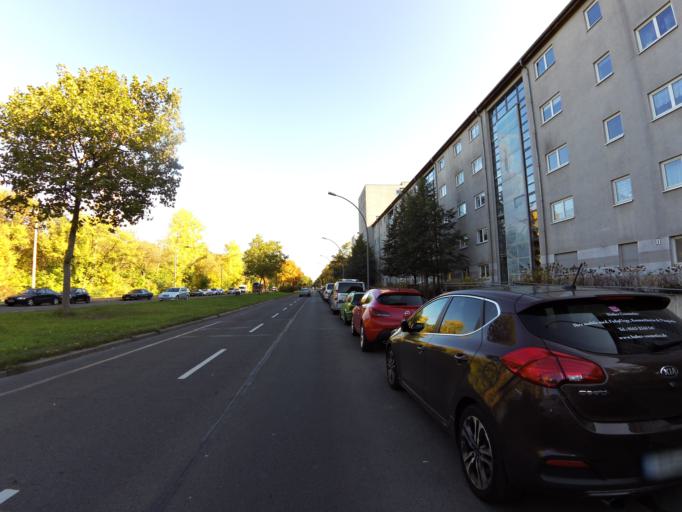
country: DE
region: Berlin
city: Oberschoneweide
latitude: 52.4631
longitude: 13.5290
